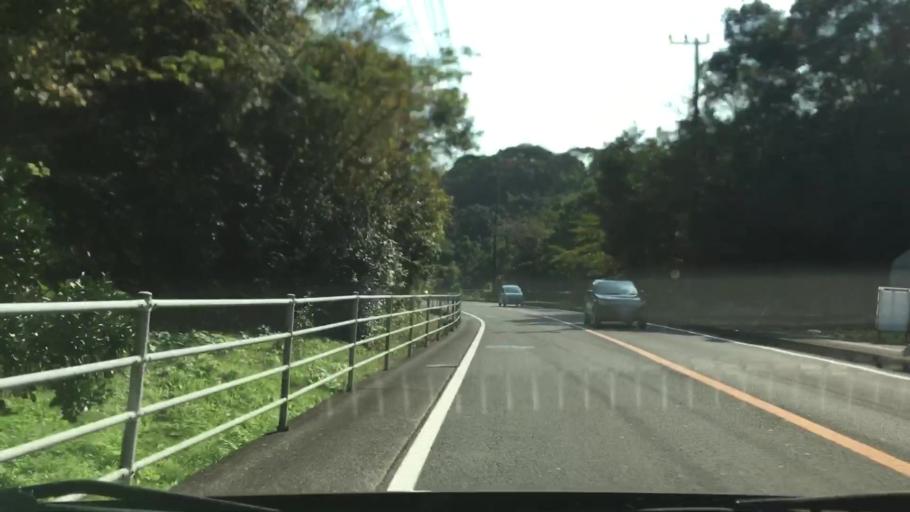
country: JP
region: Nagasaki
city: Togitsu
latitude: 32.9580
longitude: 129.7826
